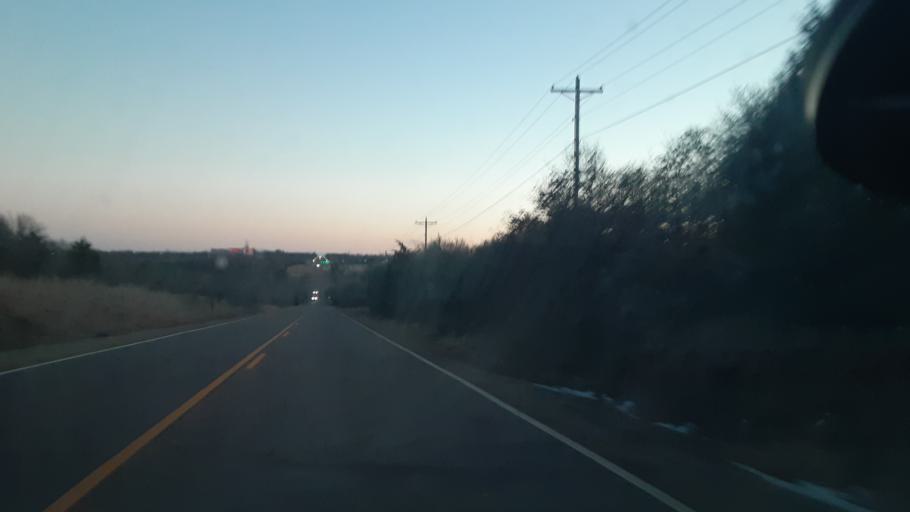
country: US
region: Oklahoma
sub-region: Oklahoma County
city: Edmond
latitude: 35.6933
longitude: -97.4251
